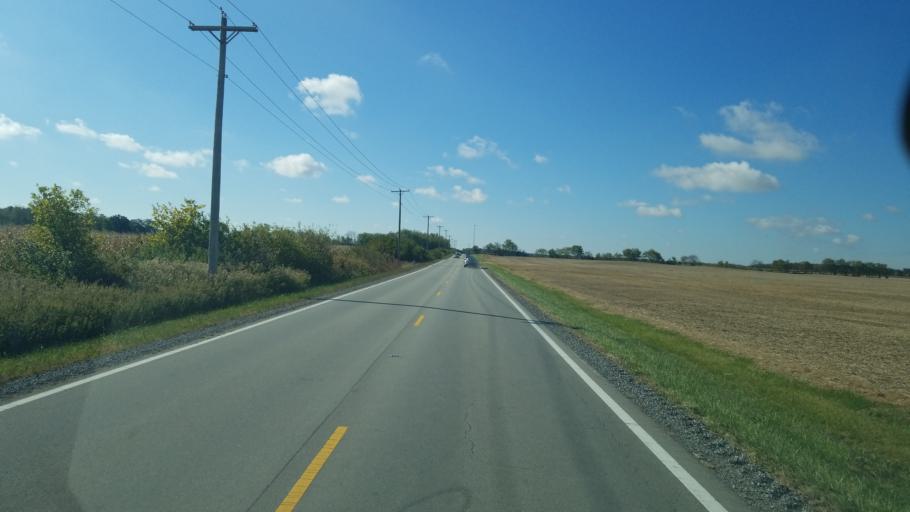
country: US
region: Ohio
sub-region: Highland County
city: Leesburg
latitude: 39.3952
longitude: -83.5349
